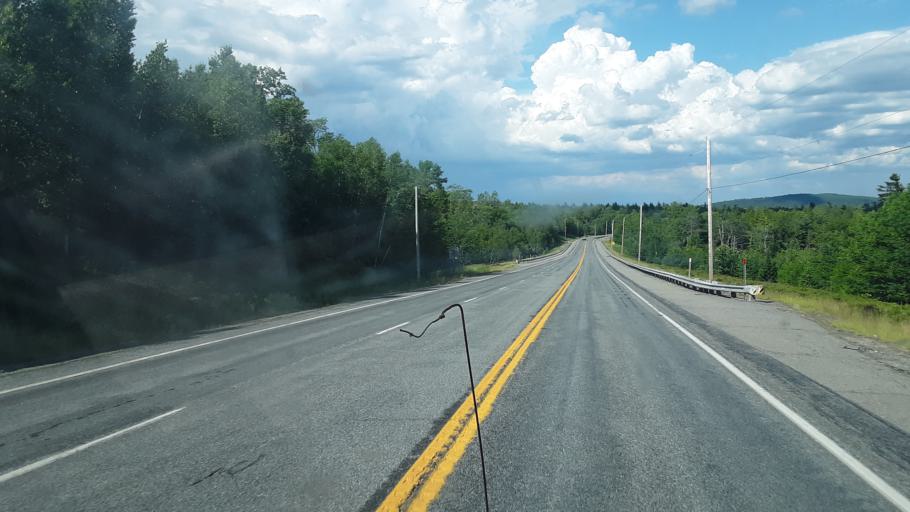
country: US
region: Maine
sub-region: Washington County
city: Cherryfield
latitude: 44.8692
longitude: -67.9980
